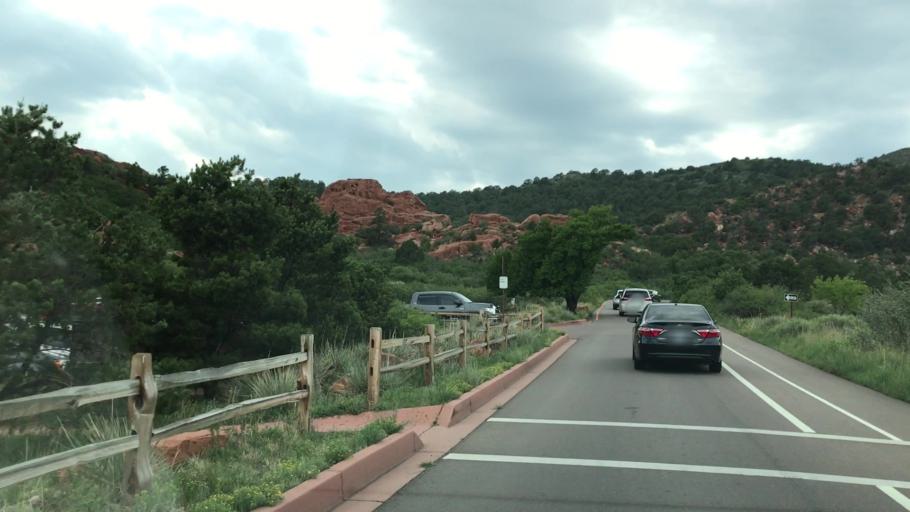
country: US
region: Colorado
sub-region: El Paso County
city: Manitou Springs
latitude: 38.8815
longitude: -104.8803
